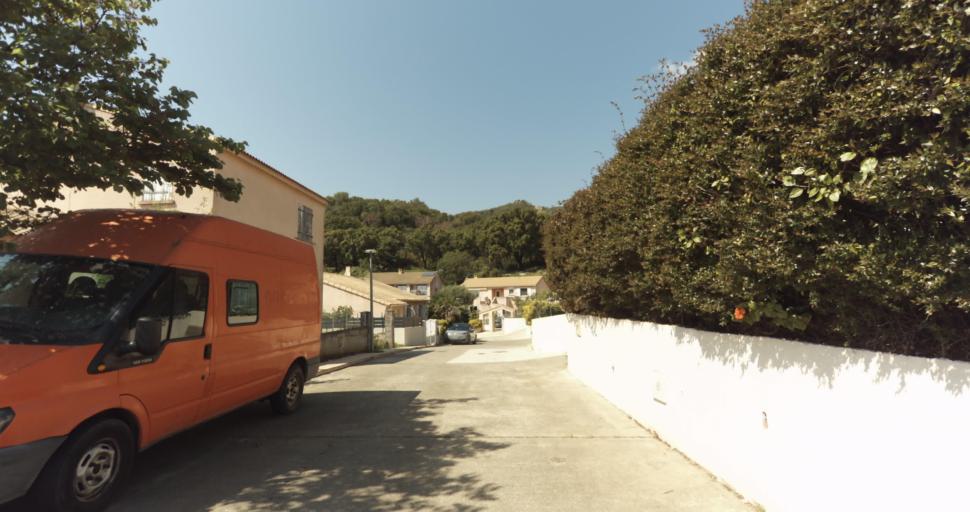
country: FR
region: Corsica
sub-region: Departement de la Haute-Corse
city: Biguglia
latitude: 42.6204
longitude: 9.4240
